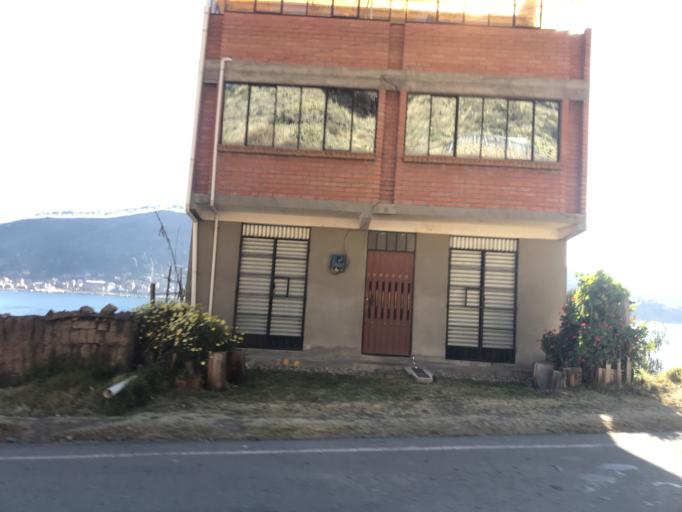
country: BO
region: La Paz
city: San Pedro
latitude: -16.2246
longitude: -68.8505
